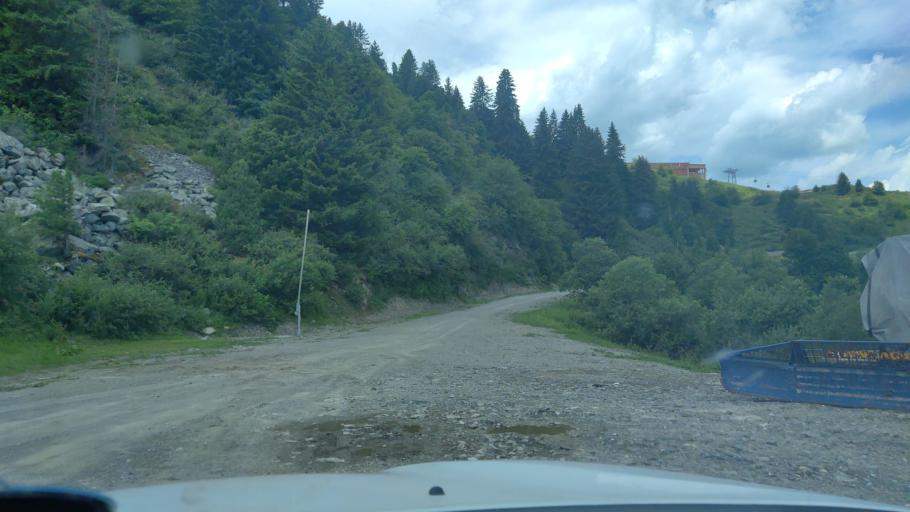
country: FR
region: Rhone-Alpes
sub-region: Departement de la Savoie
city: Meribel
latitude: 45.3739
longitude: 6.5684
